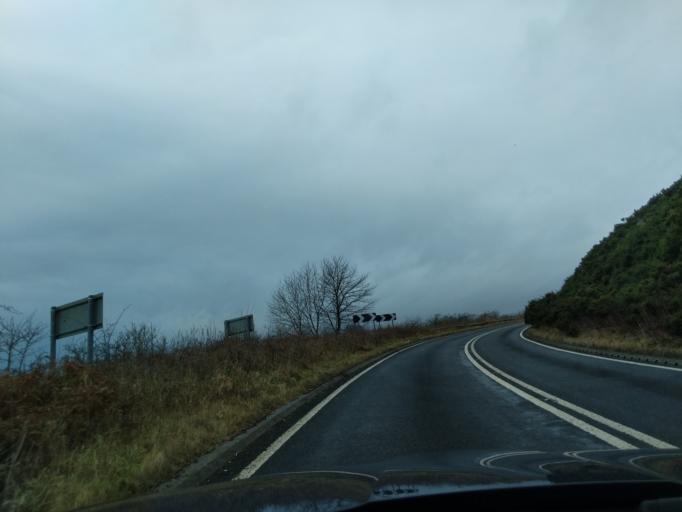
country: GB
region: England
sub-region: Northumberland
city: Rothley
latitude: 55.1599
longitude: -2.0149
